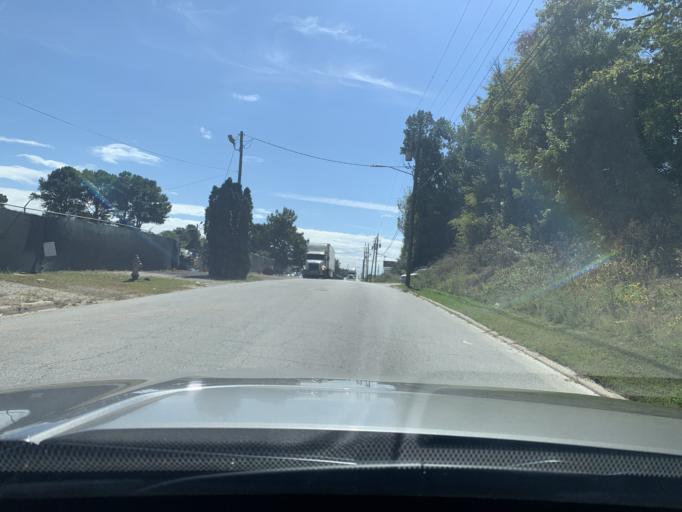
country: US
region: Georgia
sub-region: Clayton County
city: Conley
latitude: 33.6609
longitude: -84.3278
